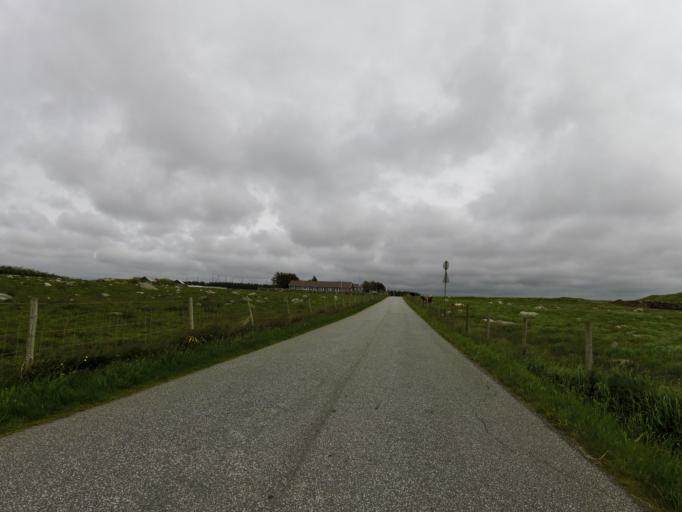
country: NO
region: Rogaland
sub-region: Ha
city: Naerbo
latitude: 58.6528
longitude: 5.5862
